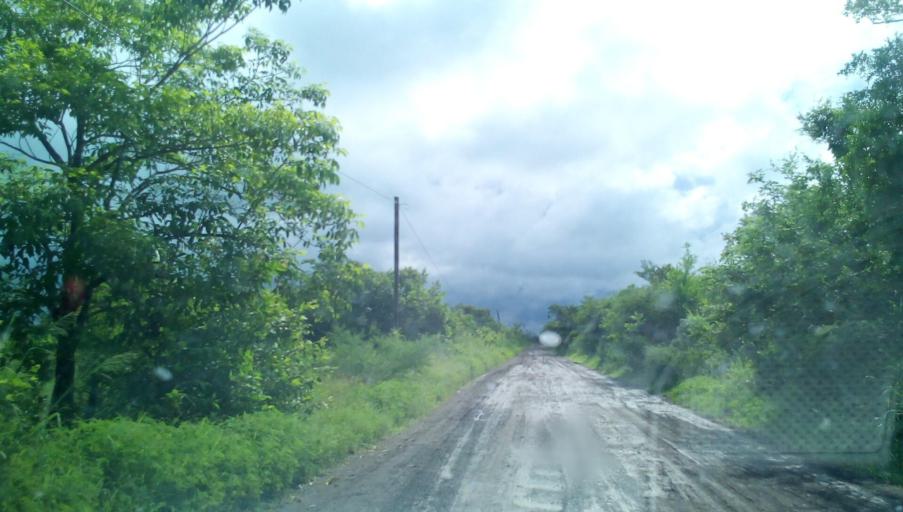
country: MX
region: Veracruz
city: Panuco
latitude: 21.8504
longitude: -98.1590
